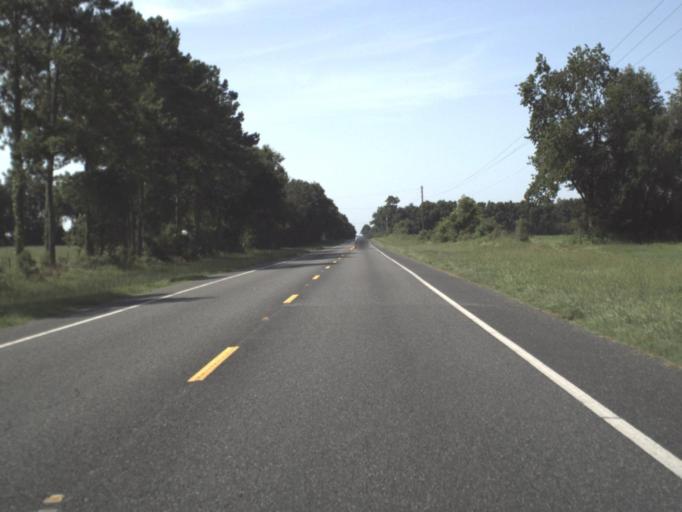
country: US
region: Florida
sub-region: Gilchrist County
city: Trenton
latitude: 29.5710
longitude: -82.8232
